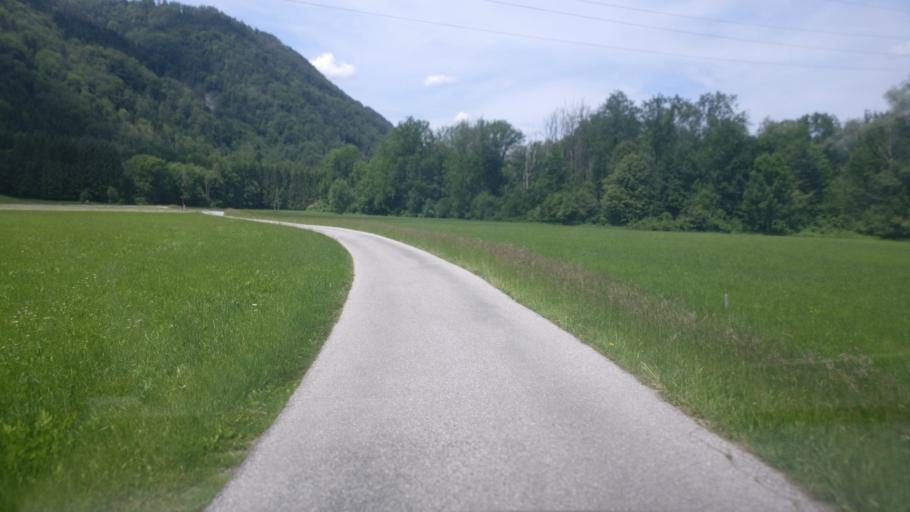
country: AT
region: Salzburg
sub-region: Politischer Bezirk Hallein
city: Kuchl
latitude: 47.6391
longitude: 13.1278
